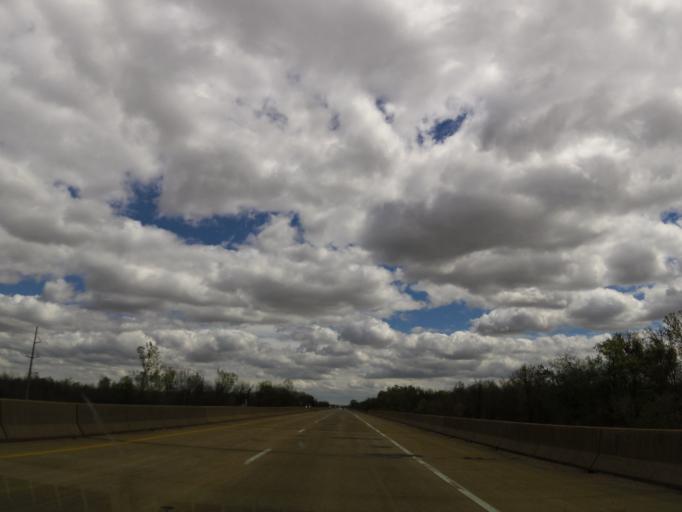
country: US
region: Arkansas
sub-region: Poinsett County
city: Marked Tree
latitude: 35.5360
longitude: -90.4793
